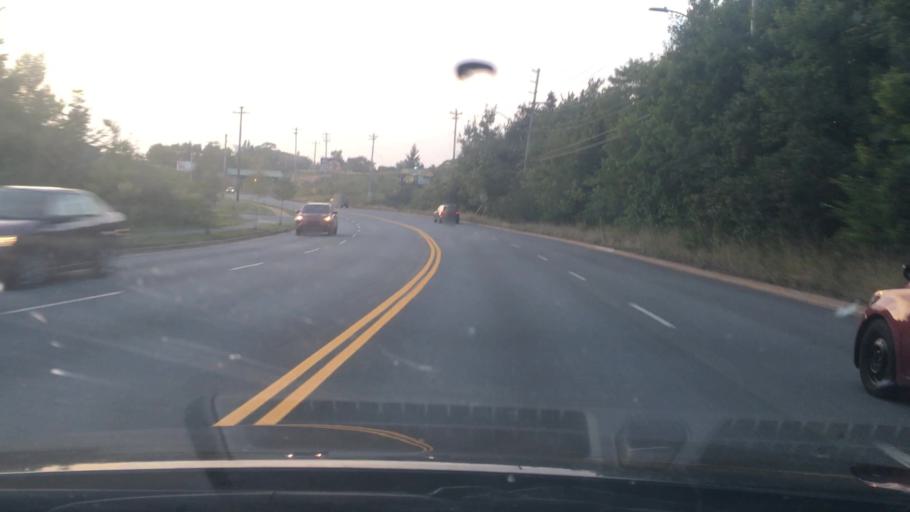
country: CA
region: Nova Scotia
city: Halifax
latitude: 44.6337
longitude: -63.5234
